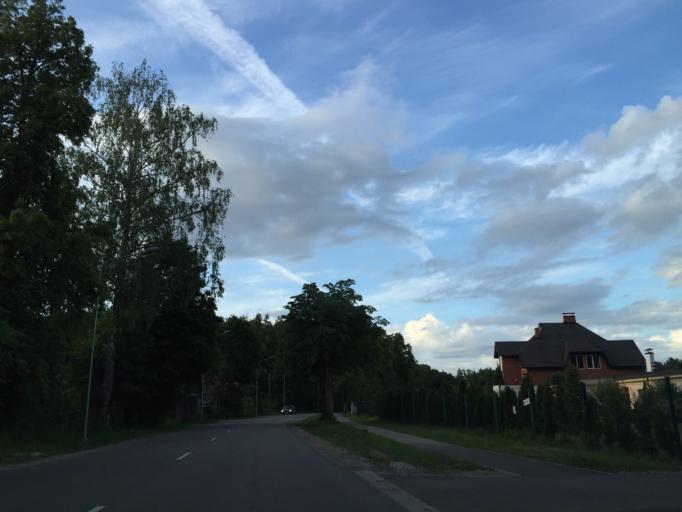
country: LV
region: Babite
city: Pinki
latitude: 56.9355
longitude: 23.8916
